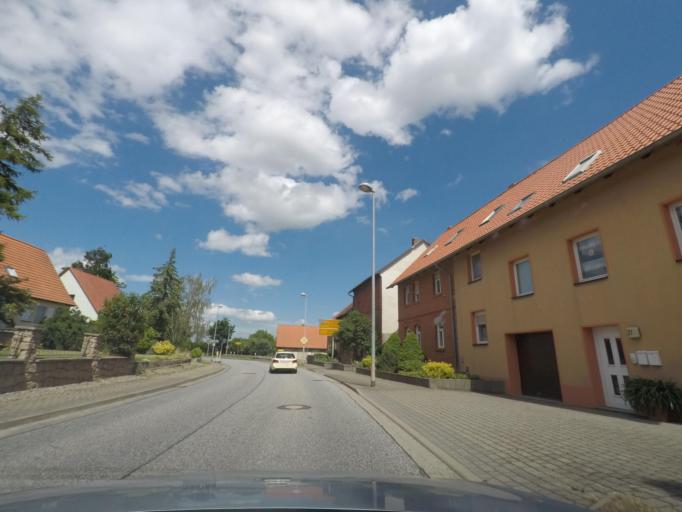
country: DE
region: Saxony-Anhalt
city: Gross Quenstedt
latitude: 51.9308
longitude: 11.1167
